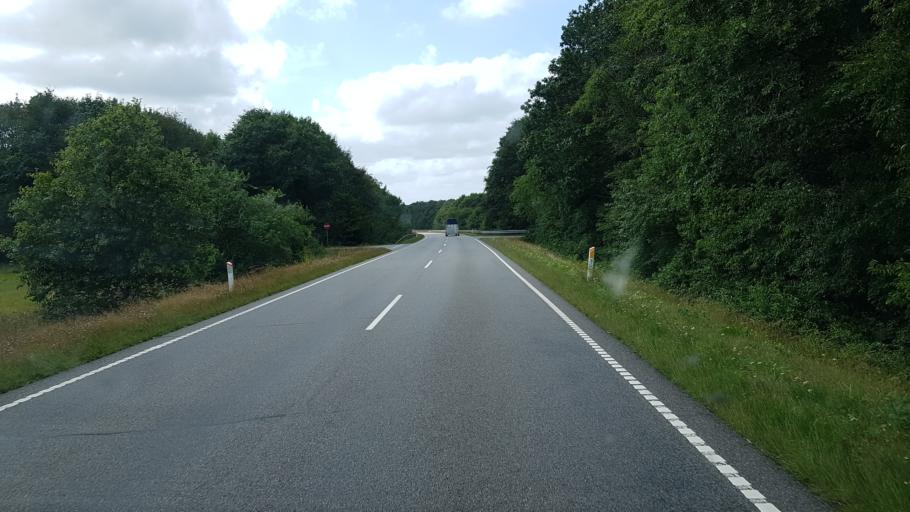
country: DK
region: South Denmark
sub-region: Vejen Kommune
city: Vejen
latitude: 55.5470
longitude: 9.0912
